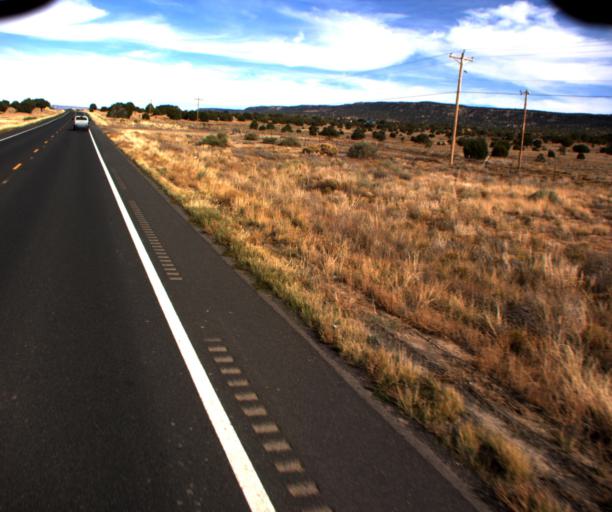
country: US
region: Arizona
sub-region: Coconino County
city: Kaibito
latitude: 36.4879
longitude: -110.6368
